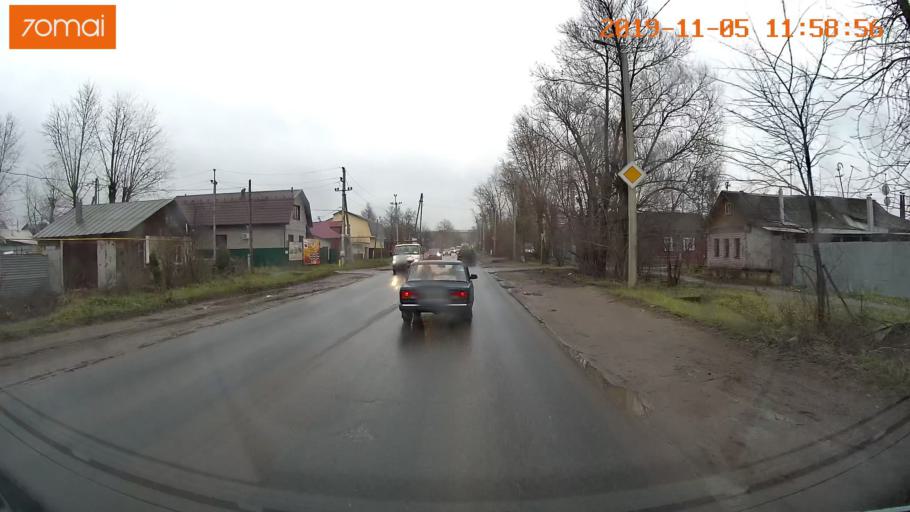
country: RU
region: Ivanovo
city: Kokhma
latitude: 56.9797
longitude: 41.0437
